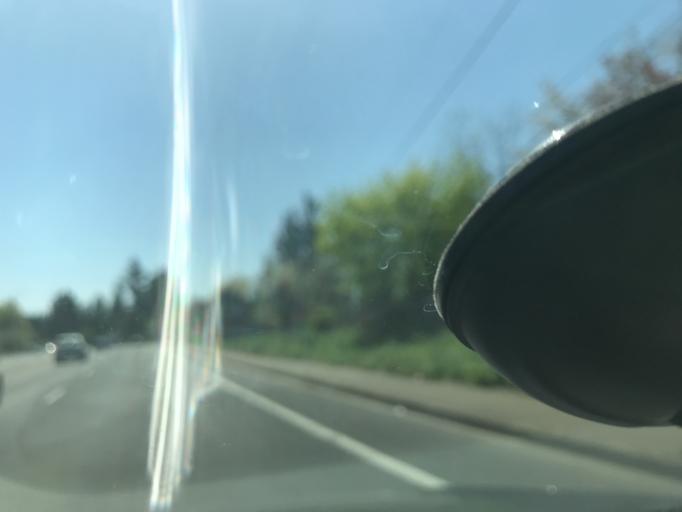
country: US
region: Oregon
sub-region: Multnomah County
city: Fairview
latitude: 45.5179
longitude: -122.4771
